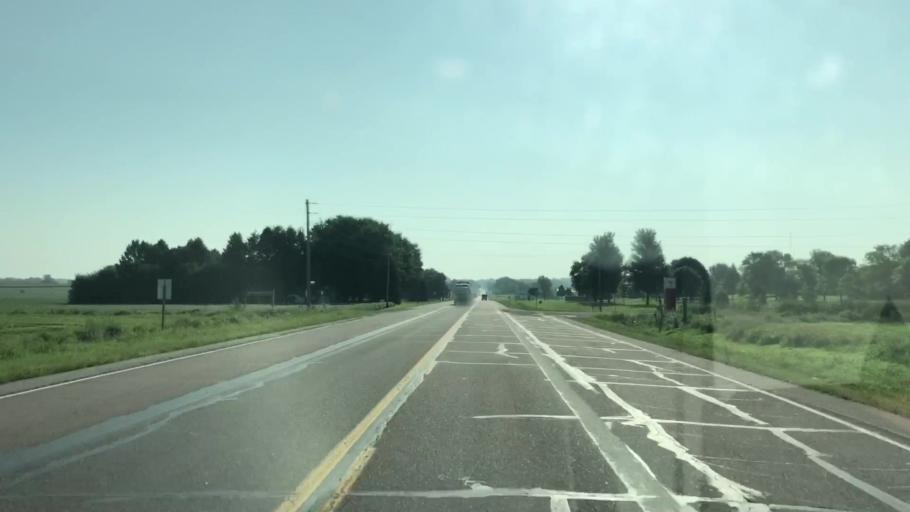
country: US
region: Iowa
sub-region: O'Brien County
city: Sheldon
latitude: 43.1859
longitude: -95.8830
